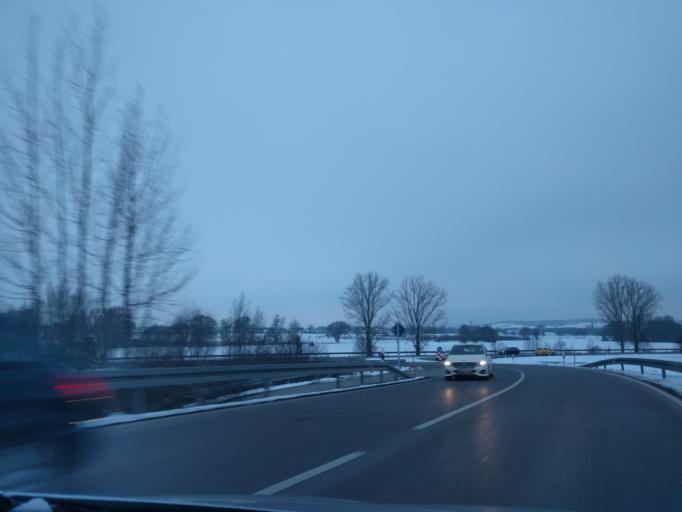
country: DE
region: Bavaria
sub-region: Swabia
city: Donauwoerth
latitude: 48.6988
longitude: 10.7938
